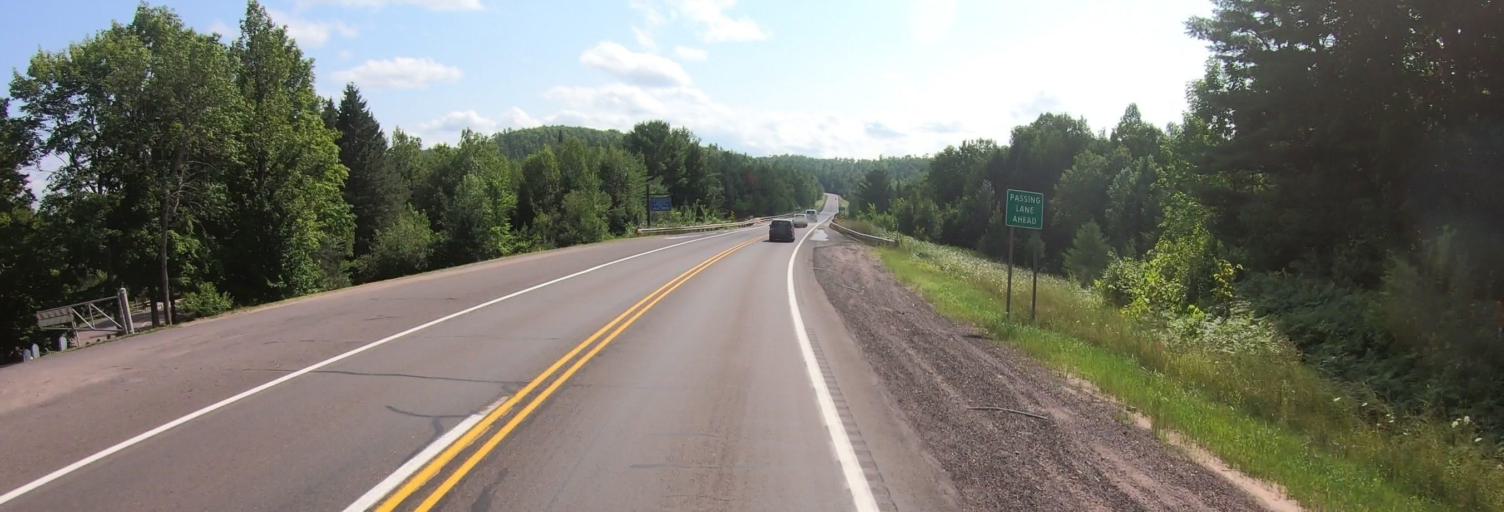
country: US
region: Michigan
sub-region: Ontonagon County
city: Ontonagon
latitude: 46.7007
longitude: -89.1590
